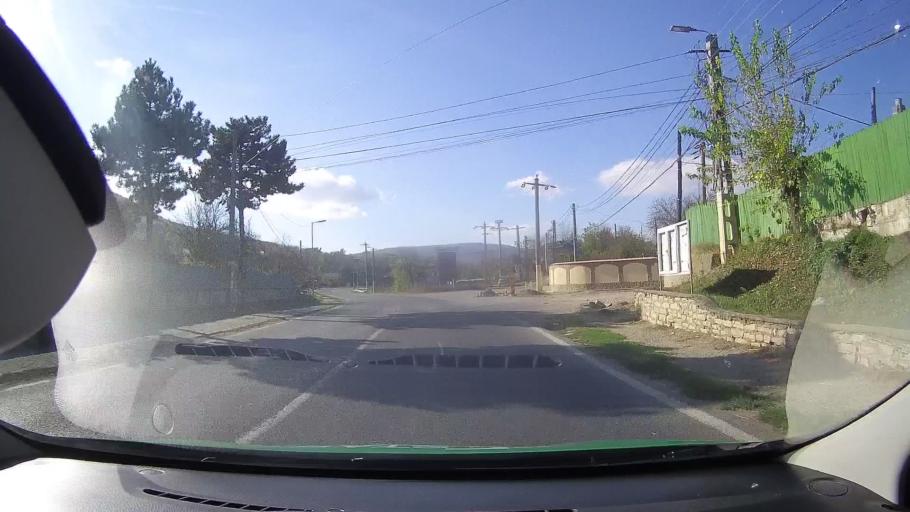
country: RO
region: Tulcea
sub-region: Oras Babadag
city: Babadag
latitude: 44.8849
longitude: 28.7016
